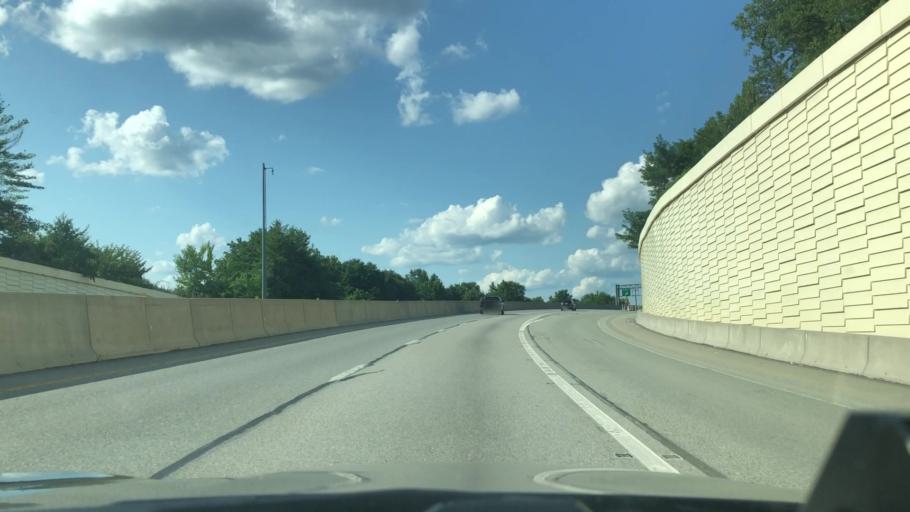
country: US
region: Pennsylvania
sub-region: Montgomery County
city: Fort Washington
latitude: 40.1454
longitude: -75.2045
